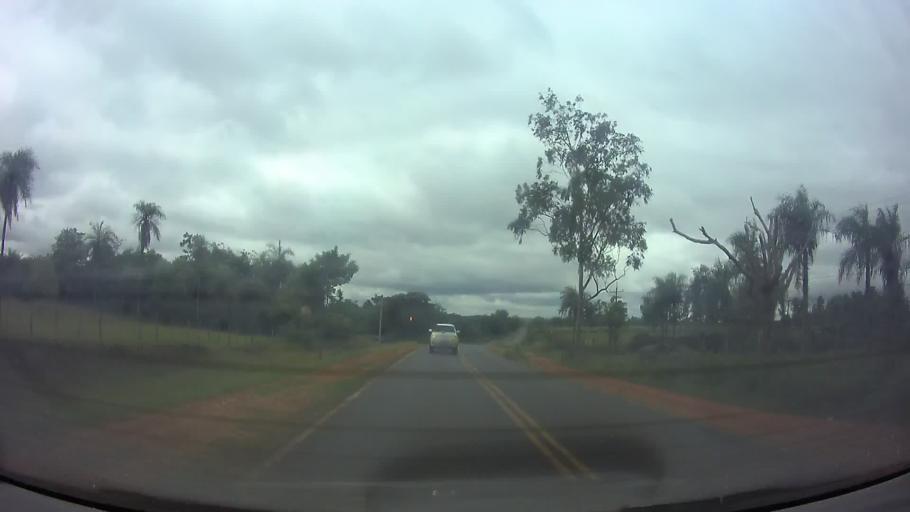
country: PY
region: Central
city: Guarambare
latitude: -25.5231
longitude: -57.4944
